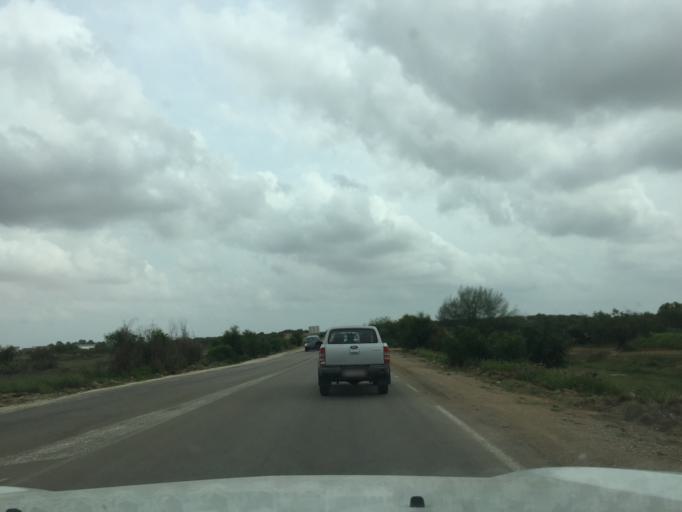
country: TN
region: Al Munastir
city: Sidi Bin Nur
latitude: 35.5432
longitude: 10.8667
